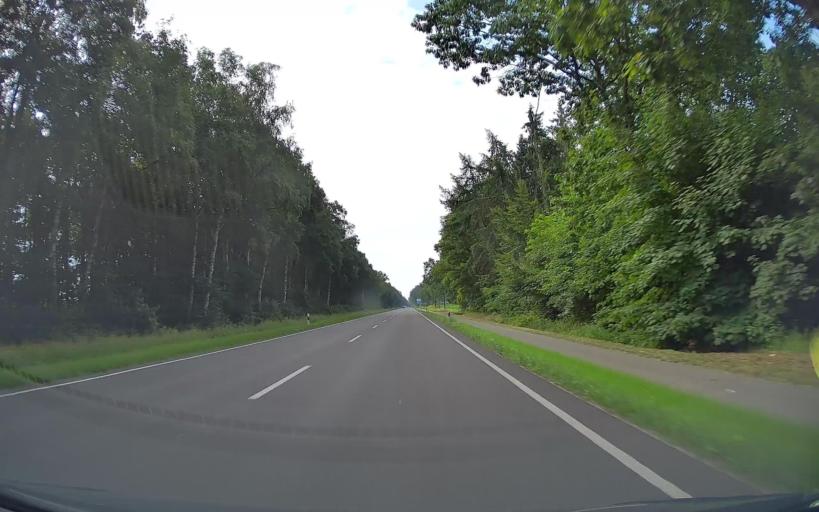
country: DE
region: Lower Saxony
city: Bosel
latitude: 52.9520
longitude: 7.9336
